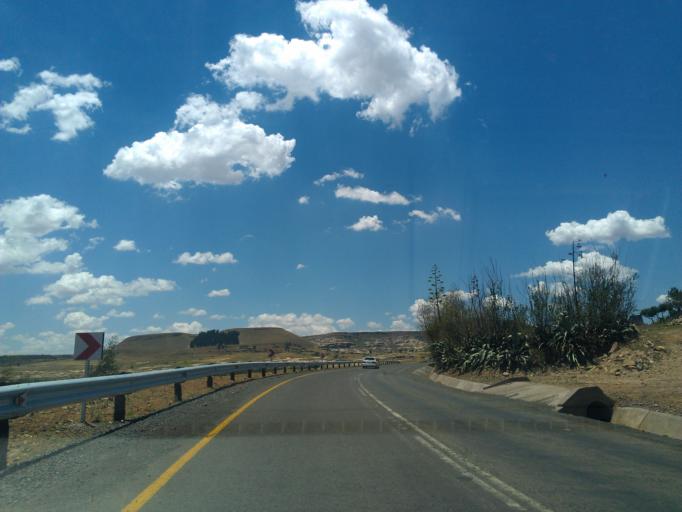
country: LS
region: Leribe
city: Maputsoe
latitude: -29.0912
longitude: 27.9596
